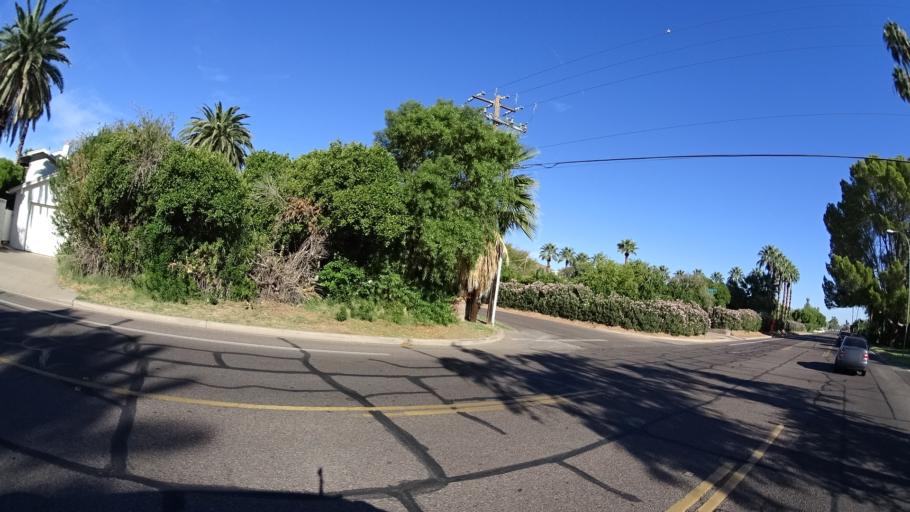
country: US
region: Arizona
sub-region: Maricopa County
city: Paradise Valley
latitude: 33.4982
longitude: -111.9347
